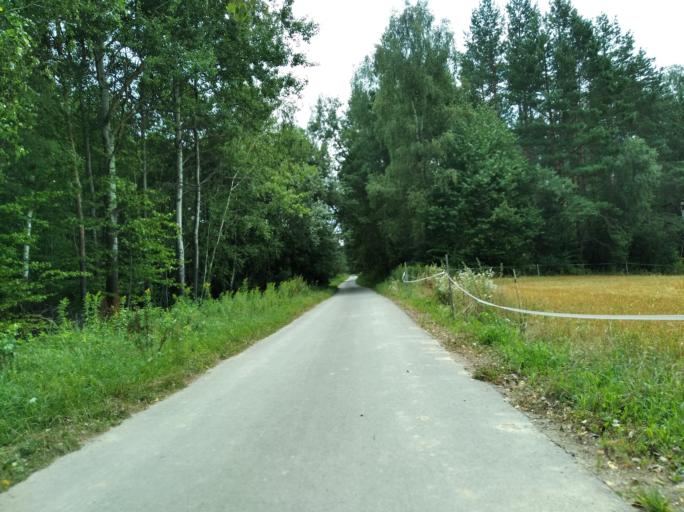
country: PL
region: Subcarpathian Voivodeship
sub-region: Powiat krosnienski
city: Odrzykon
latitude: 49.7831
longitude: 21.7190
